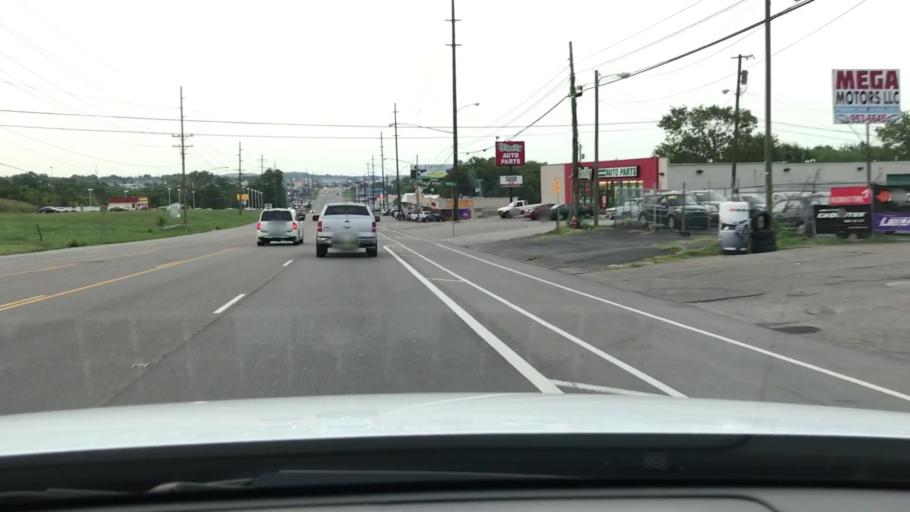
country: US
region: Tennessee
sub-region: Davidson County
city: Goodlettsville
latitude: 36.2802
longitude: -86.7083
